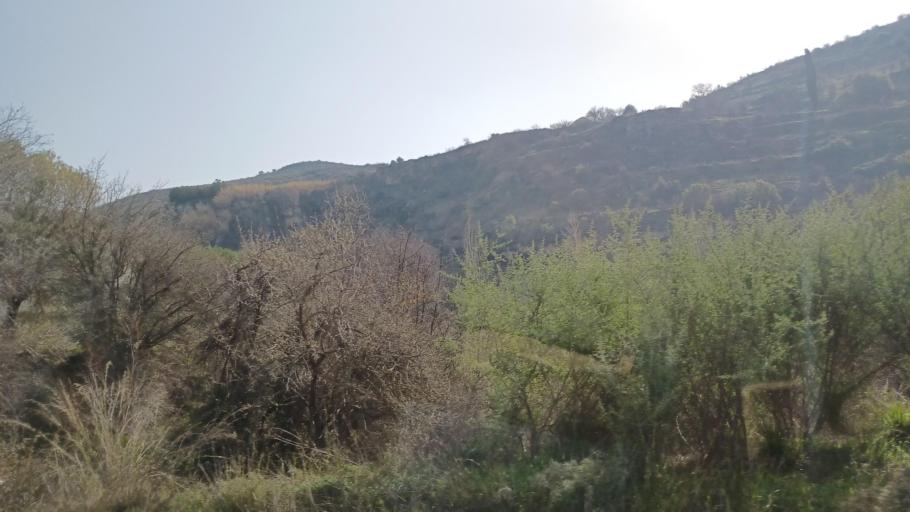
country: CY
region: Limassol
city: Pachna
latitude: 34.8146
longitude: 32.7421
